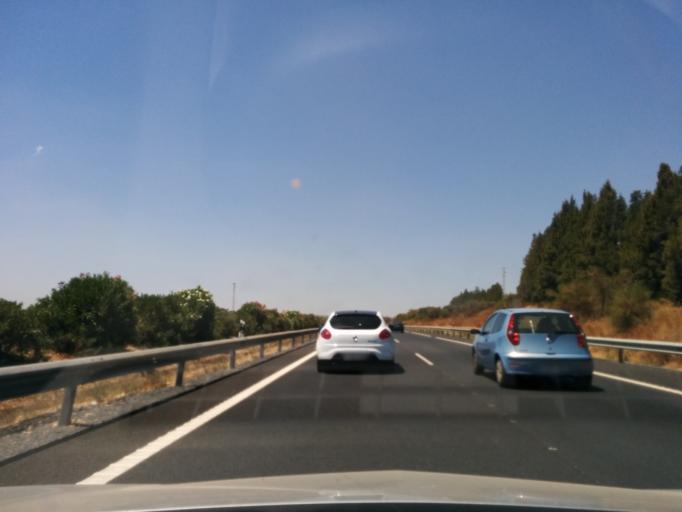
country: ES
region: Andalusia
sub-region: Provincia de Huelva
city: Lucena del Puerto
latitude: 37.3401
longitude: -6.7420
